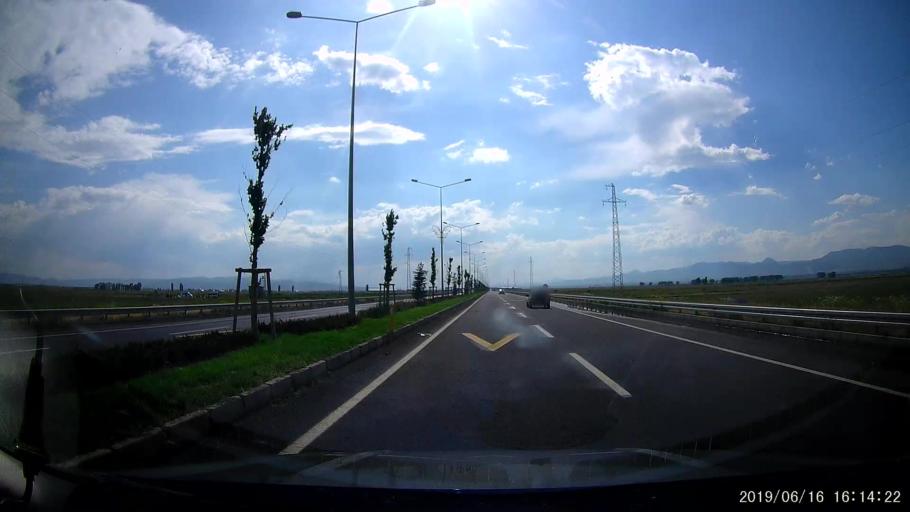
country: TR
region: Erzurum
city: Erzurum
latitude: 39.9606
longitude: 41.2508
